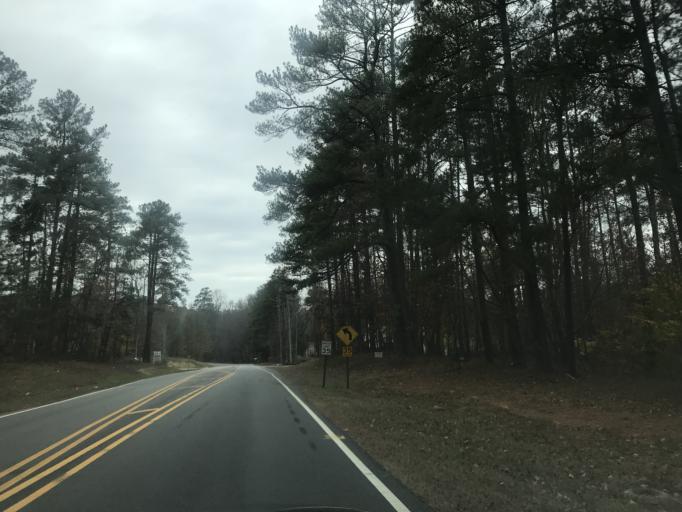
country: US
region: North Carolina
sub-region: Franklin County
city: Youngsville
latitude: 36.0169
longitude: -78.4889
